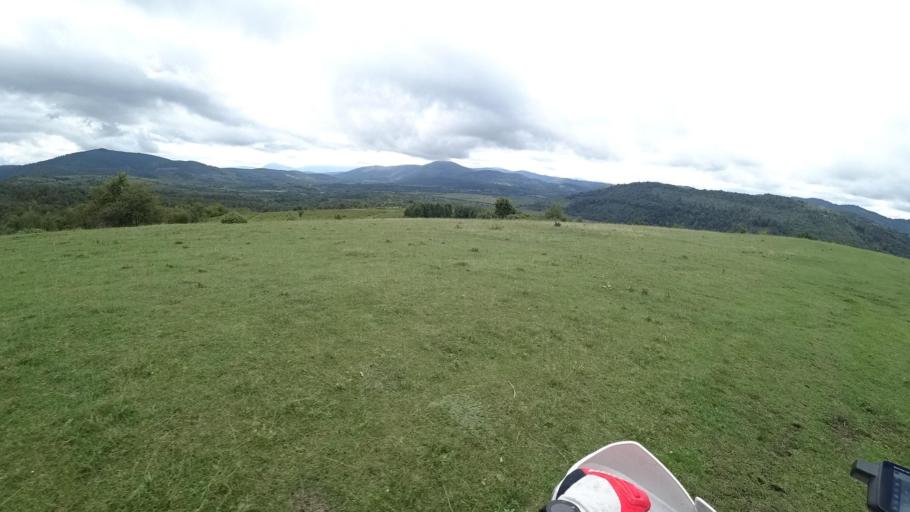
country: BA
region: Republika Srpska
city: Bronzani Majdan
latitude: 44.6965
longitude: 16.9848
